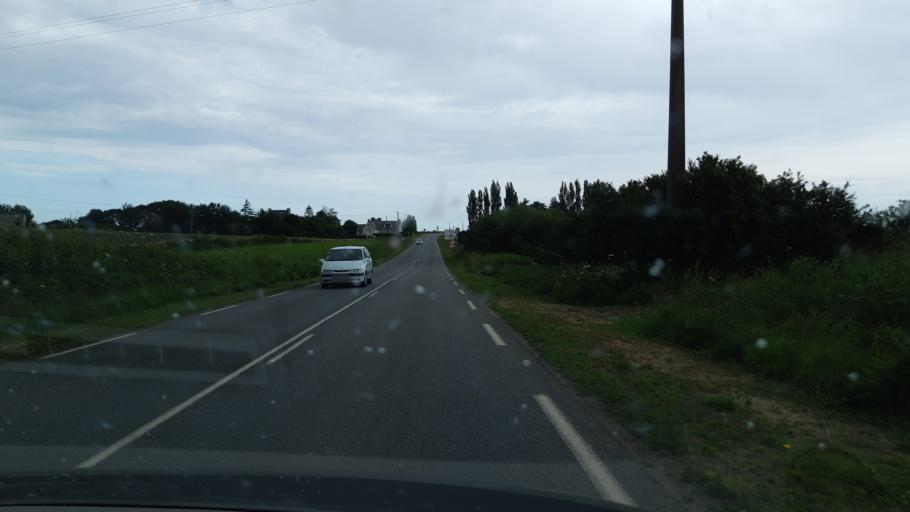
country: FR
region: Brittany
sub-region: Departement du Finistere
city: Plougoulm
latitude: 48.6407
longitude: -4.0510
